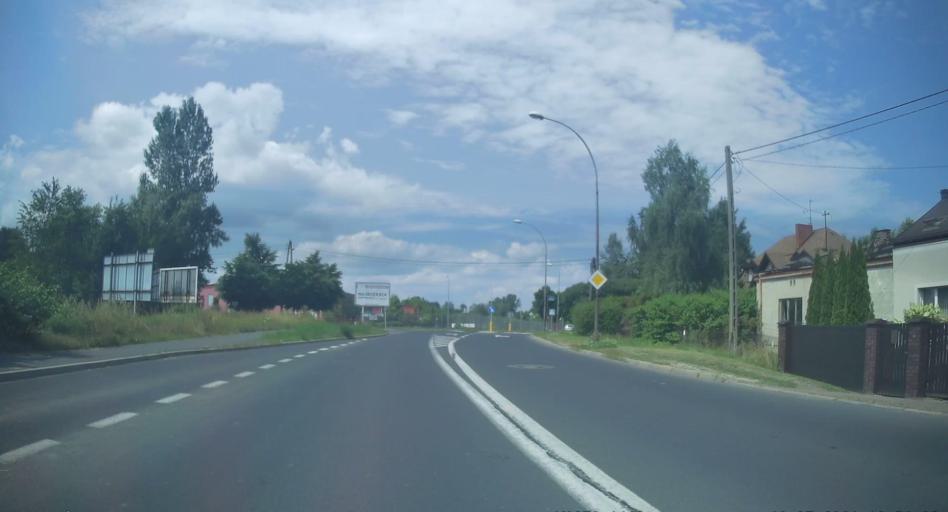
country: PL
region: Silesian Voivodeship
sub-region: Czestochowa
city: Czestochowa
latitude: 50.8040
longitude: 19.0811
